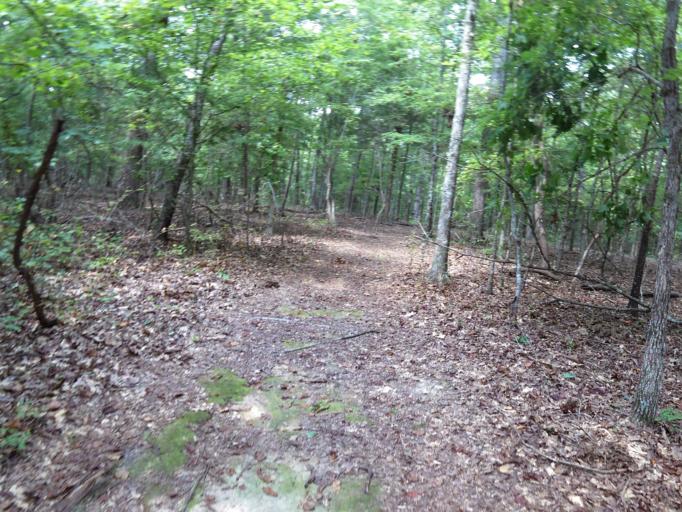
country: US
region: Tennessee
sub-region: Hardin County
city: Crump
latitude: 35.1466
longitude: -88.3240
